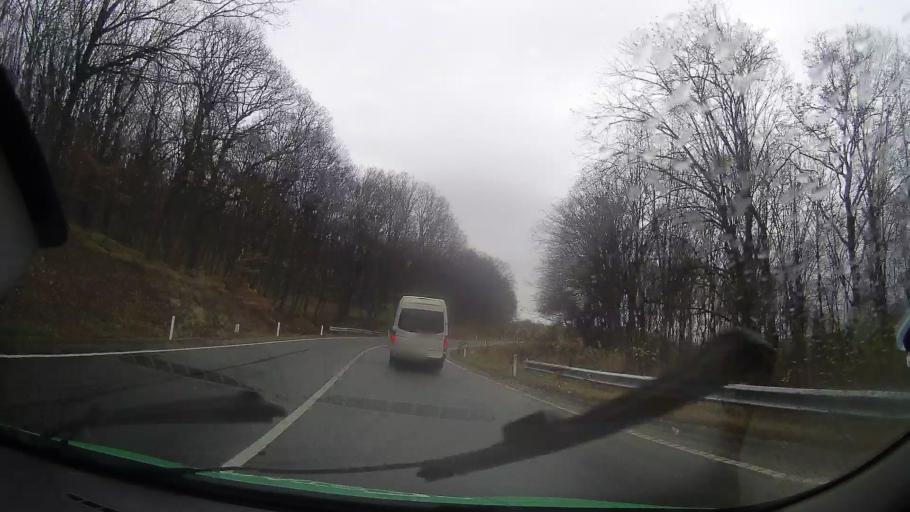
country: RO
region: Bistrita-Nasaud
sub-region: Comuna Sieu-Magherus
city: Sieu-Magherus
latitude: 47.0413
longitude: 24.4202
